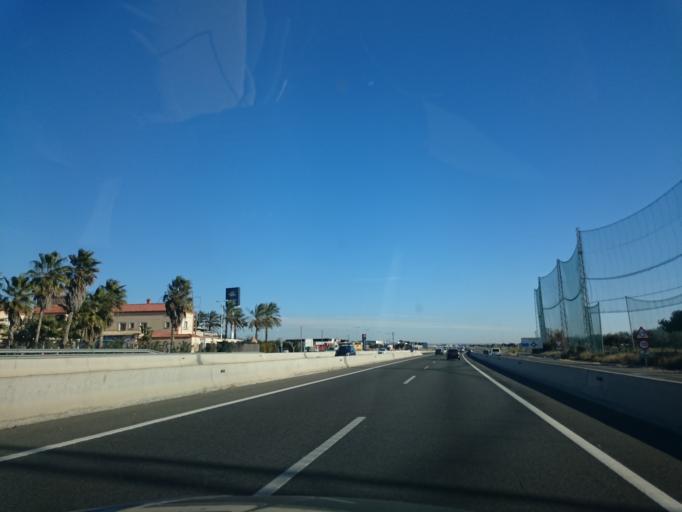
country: ES
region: Catalonia
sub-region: Provincia de Tarragona
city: Cambrils
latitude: 41.0897
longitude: 1.0932
